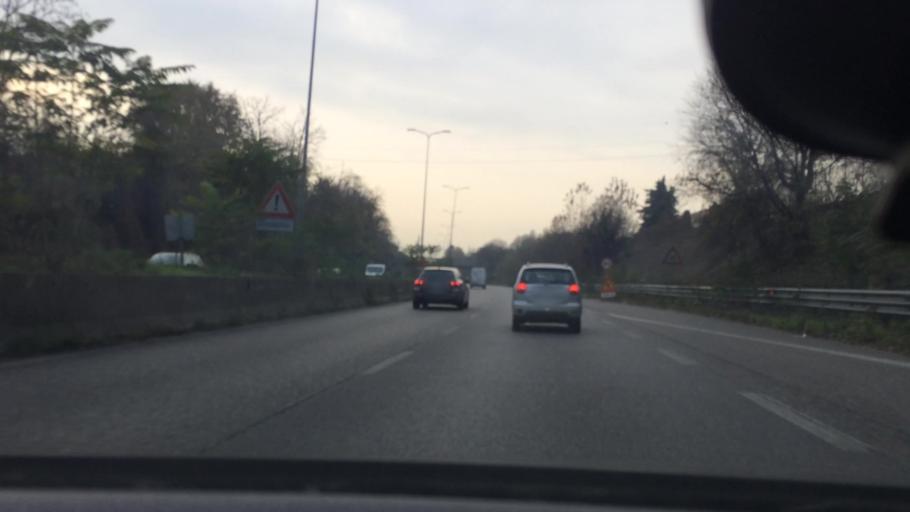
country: IT
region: Lombardy
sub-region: Citta metropolitana di Milano
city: Cormano
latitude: 45.5436
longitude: 9.1616
